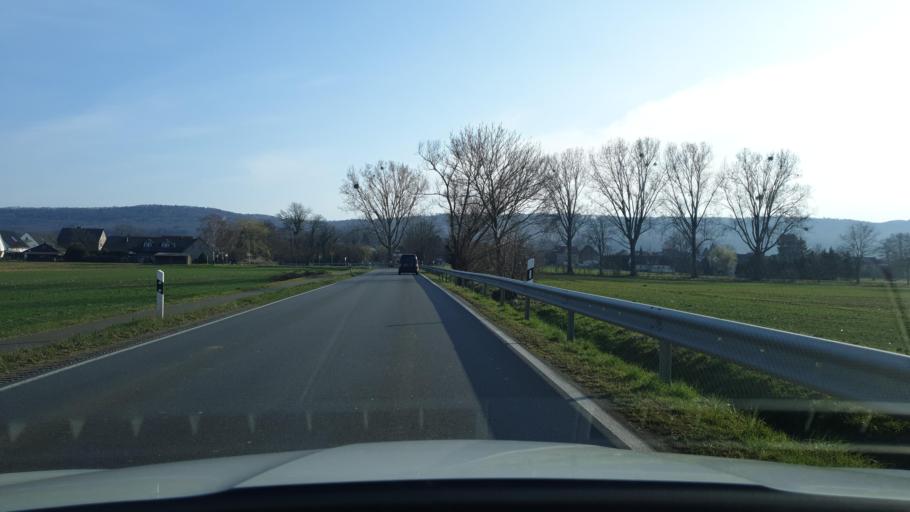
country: DE
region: North Rhine-Westphalia
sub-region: Regierungsbezirk Detmold
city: Minden
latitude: 52.2768
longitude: 8.8629
